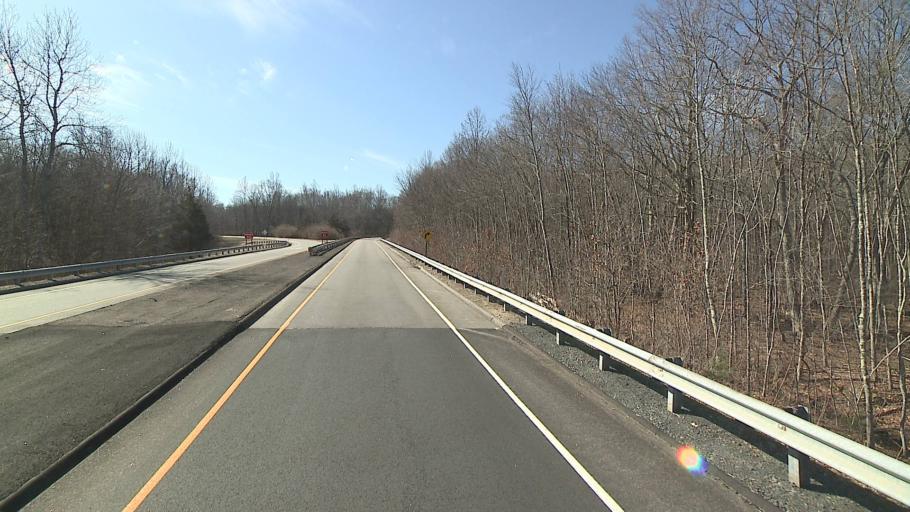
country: US
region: Connecticut
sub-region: New London County
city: Colchester
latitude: 41.5746
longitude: -72.2949
